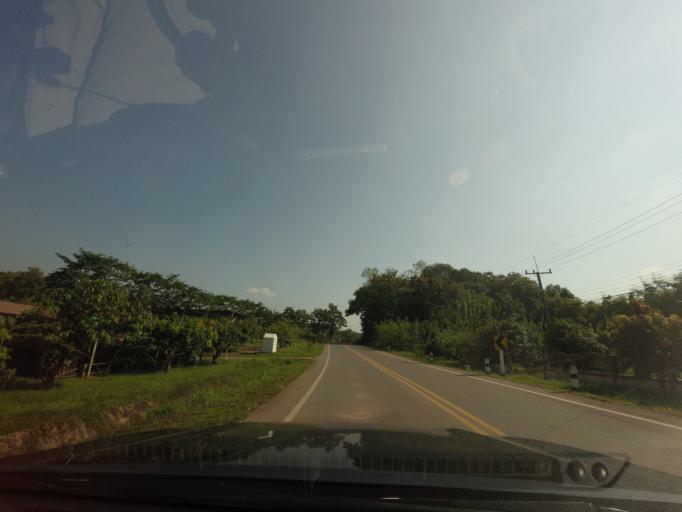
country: TH
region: Nan
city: Nan
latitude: 18.8480
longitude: 100.8131
